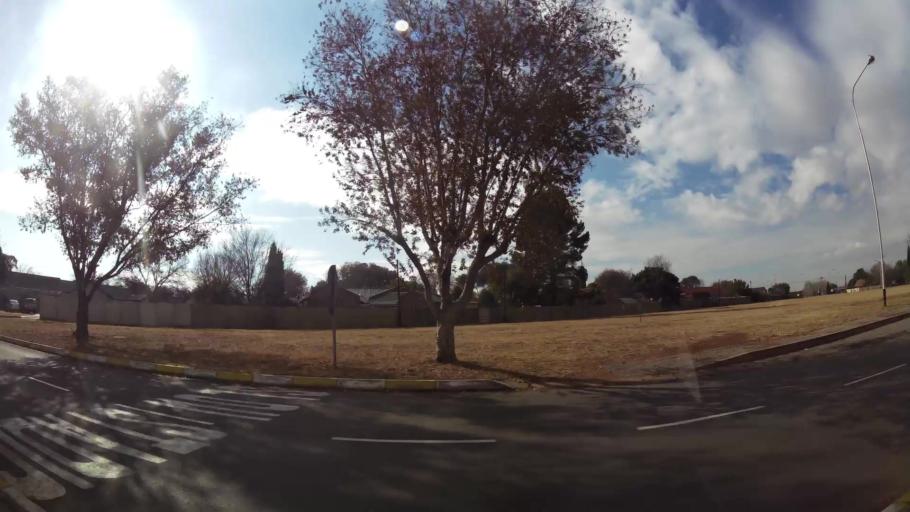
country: ZA
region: Gauteng
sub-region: Sedibeng District Municipality
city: Meyerton
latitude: -26.5551
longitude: 28.0319
